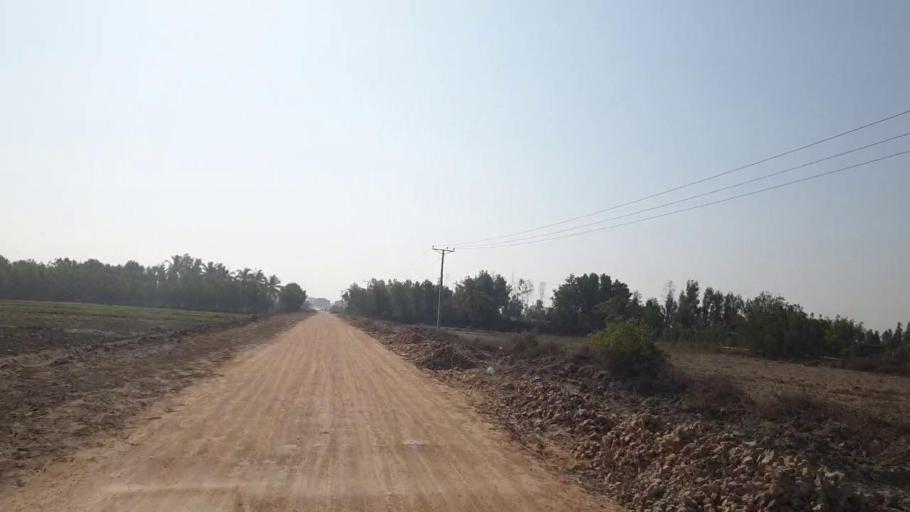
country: PK
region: Sindh
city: Thatta
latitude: 24.7641
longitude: 67.9144
